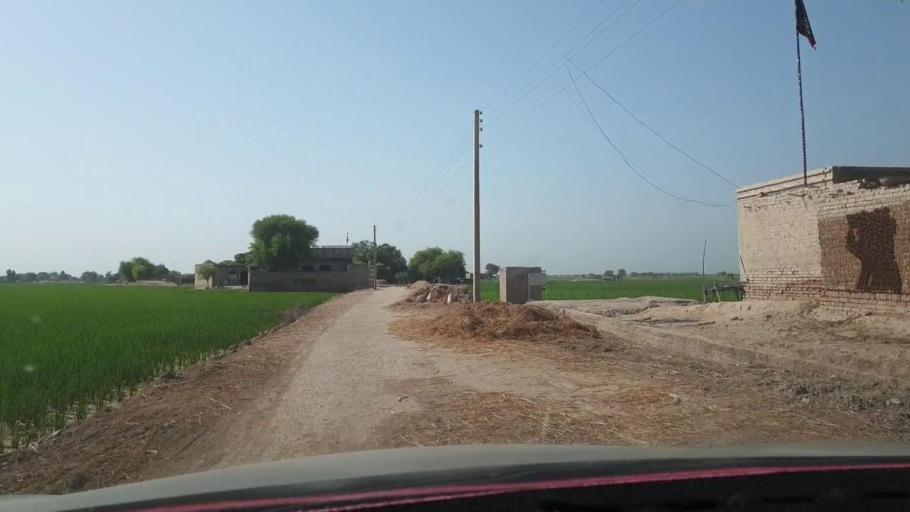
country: PK
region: Sindh
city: Nasirabad
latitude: 27.3820
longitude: 67.8801
